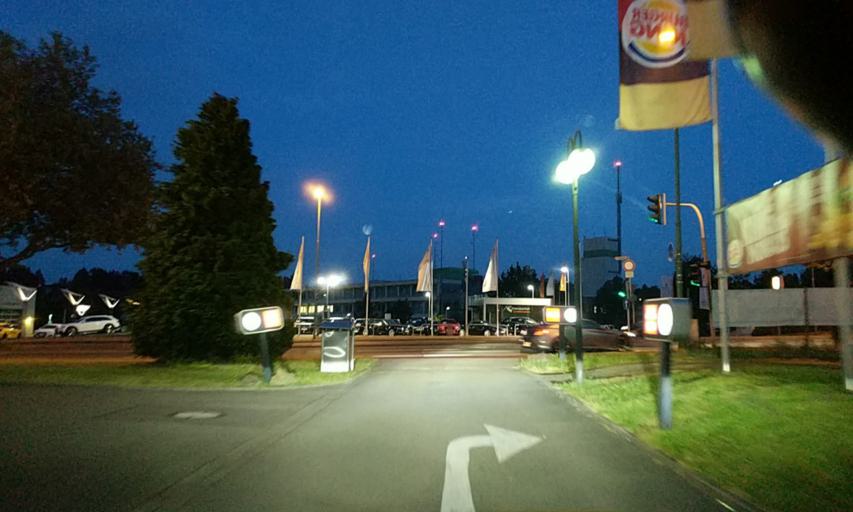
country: DE
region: Rheinland-Pfalz
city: Kaiserslautern
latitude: 49.4404
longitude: 7.7412
